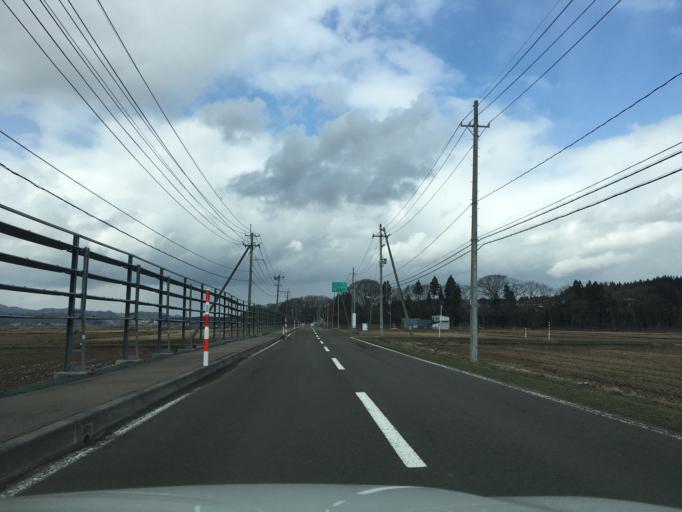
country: JP
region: Akita
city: Takanosu
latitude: 40.1400
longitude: 140.3507
